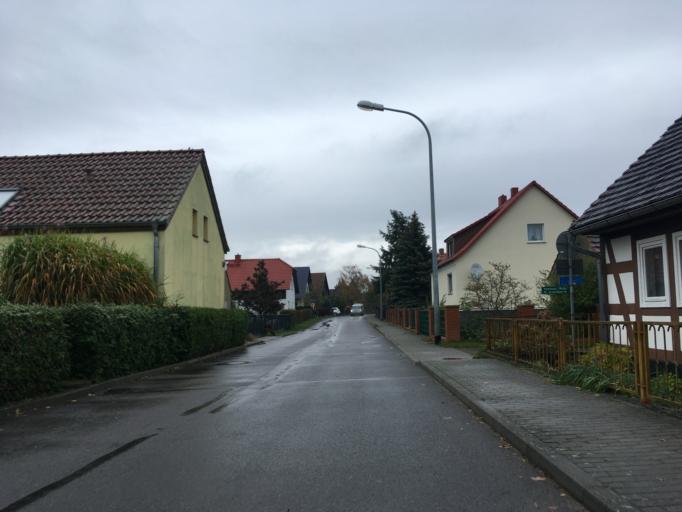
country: DE
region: Brandenburg
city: Friedland
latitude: 52.0420
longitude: 14.1822
